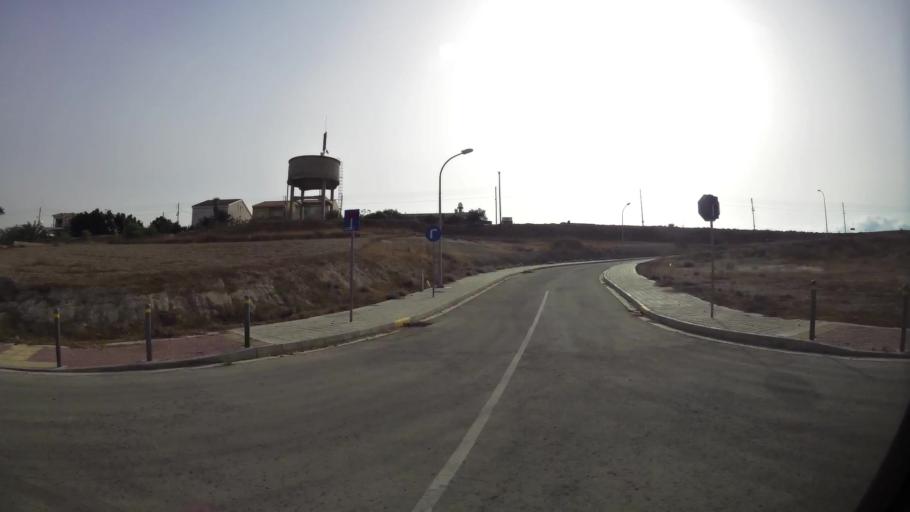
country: CY
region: Lefkosia
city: Geri
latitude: 35.0693
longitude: 33.3899
